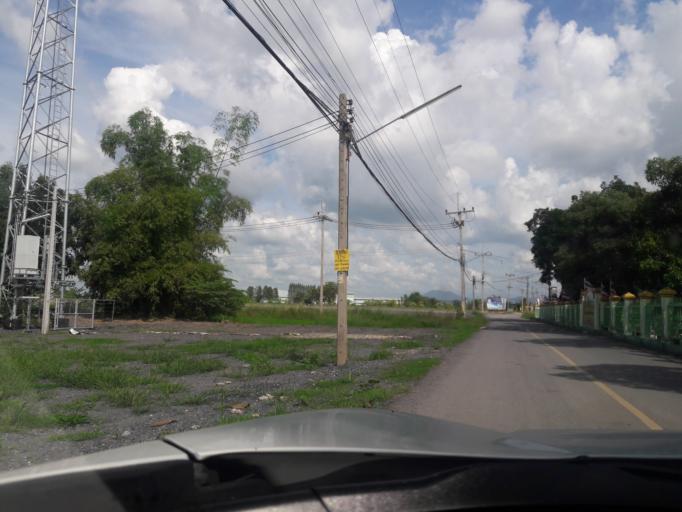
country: TH
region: Lop Buri
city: Ban Mi
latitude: 14.9711
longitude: 100.5251
